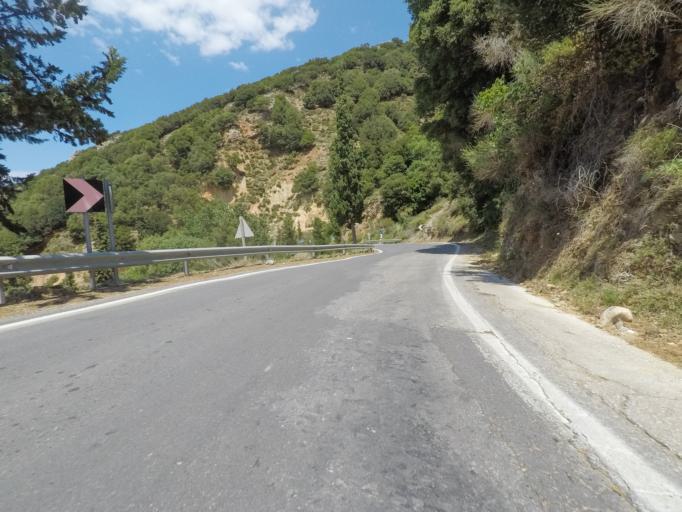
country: GR
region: Crete
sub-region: Nomos Irakleiou
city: Mokhos
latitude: 35.2244
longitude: 25.4626
